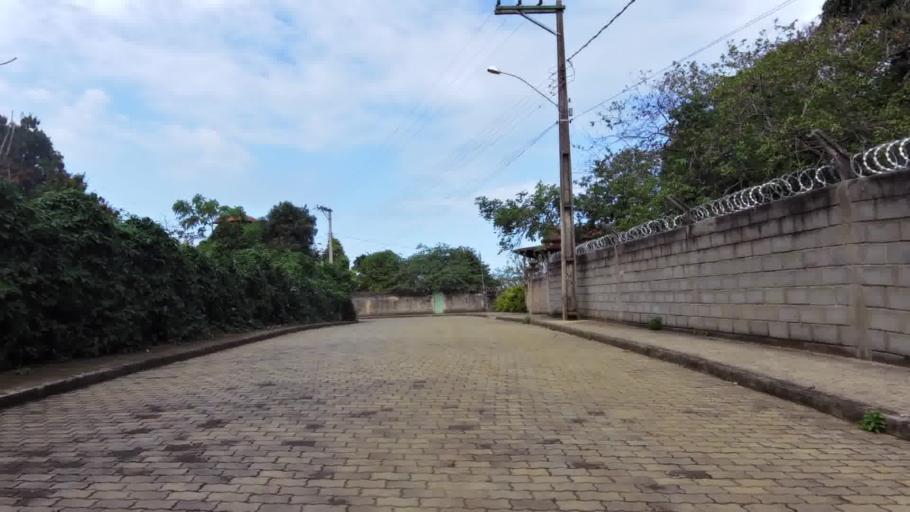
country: BR
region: Espirito Santo
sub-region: Piuma
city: Piuma
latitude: -20.8307
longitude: -40.6988
